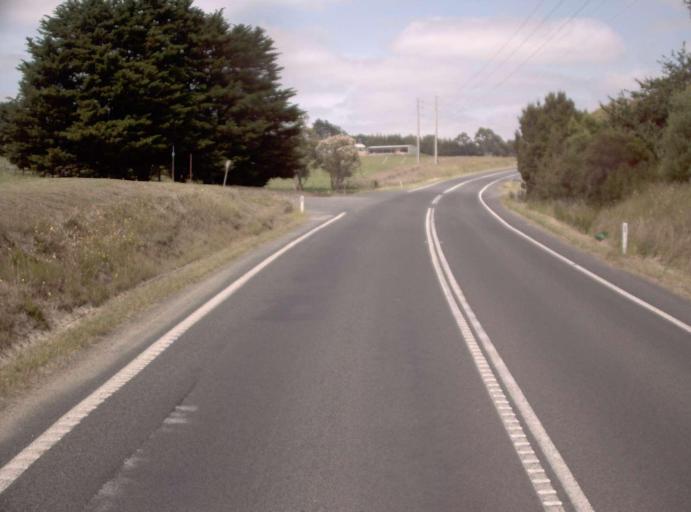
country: AU
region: Victoria
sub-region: Baw Baw
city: Warragul
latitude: -38.4406
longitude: 146.0347
